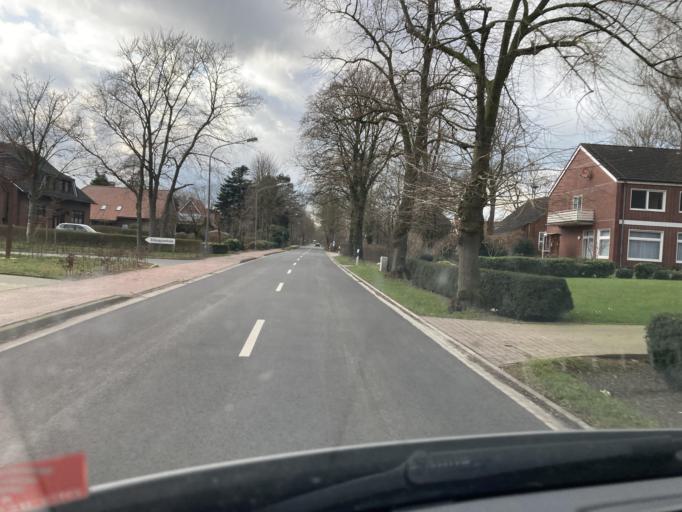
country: DE
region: Lower Saxony
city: Filsum
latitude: 53.1865
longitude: 7.6131
